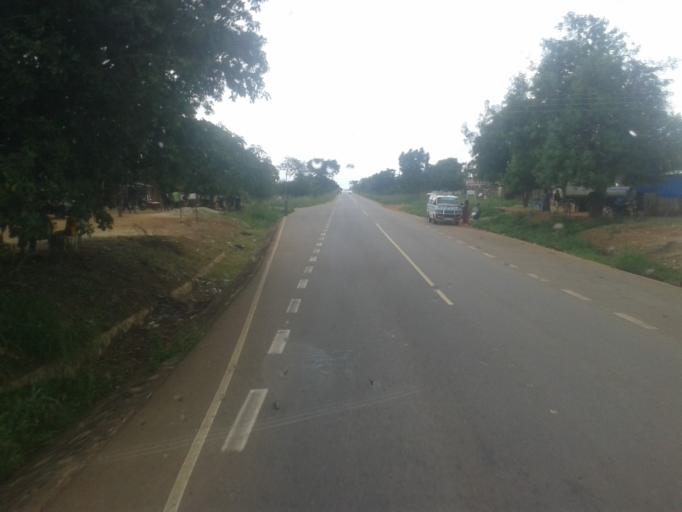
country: UG
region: Central Region
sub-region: Nakasongola District
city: Nakasongola
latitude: 1.3559
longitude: 32.3749
